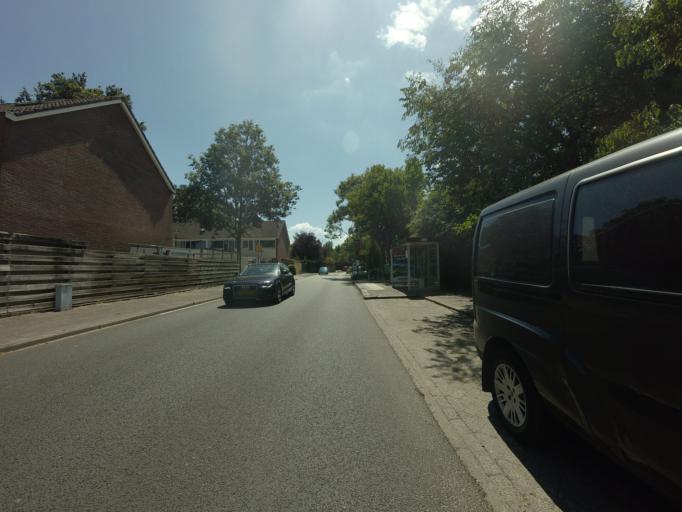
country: NL
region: Utrecht
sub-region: Gemeente Soest
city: Soest
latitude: 52.1668
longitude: 5.2832
